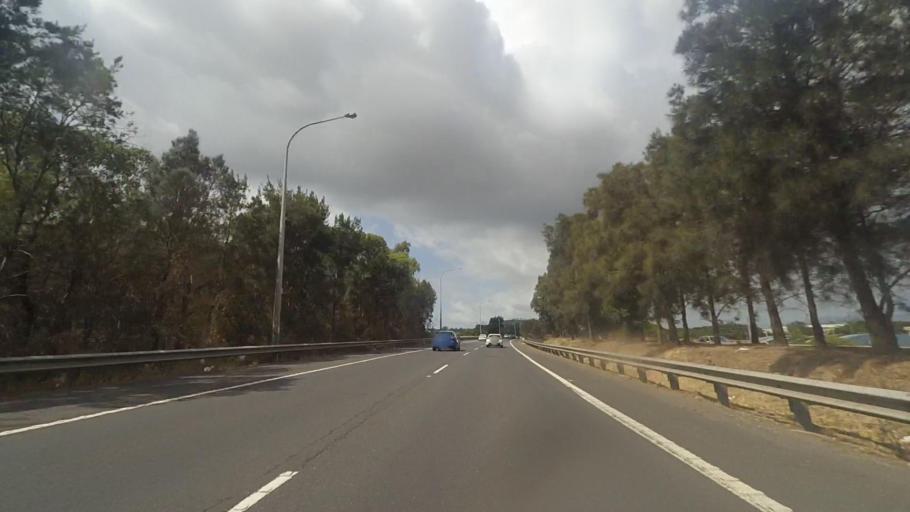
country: AU
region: New South Wales
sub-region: Wollongong
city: Mount Saint Thomas
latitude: -34.4529
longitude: 150.8590
